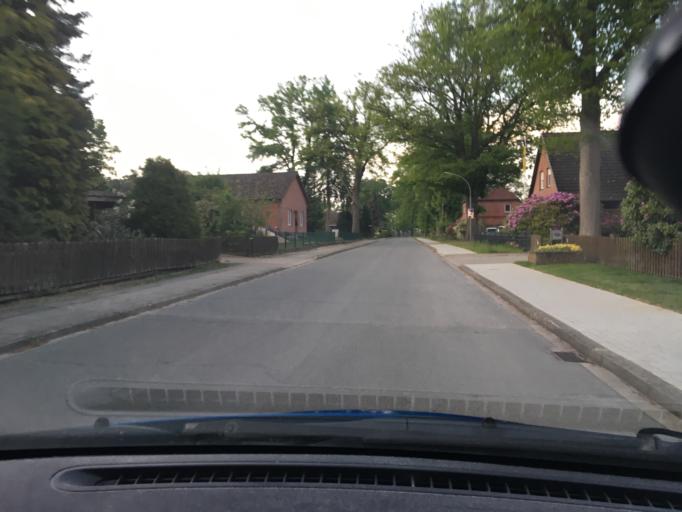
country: DE
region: Lower Saxony
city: Garstedt
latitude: 53.2822
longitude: 10.1595
